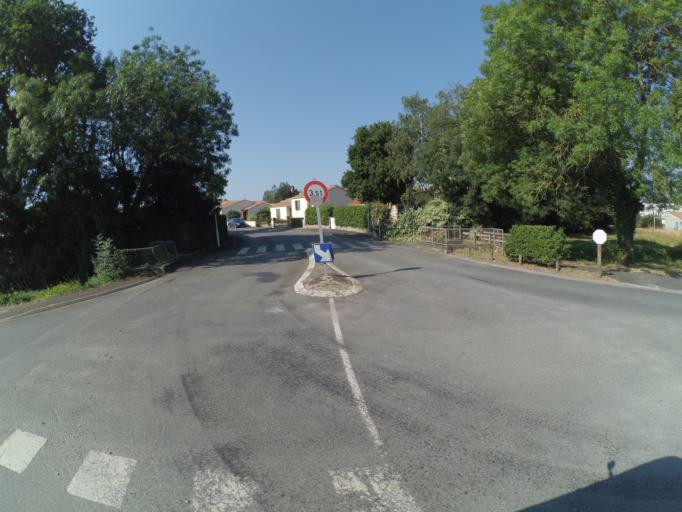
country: FR
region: Pays de la Loire
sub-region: Departement de la Vendee
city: Treize-Septiers
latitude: 46.9867
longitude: -1.2249
